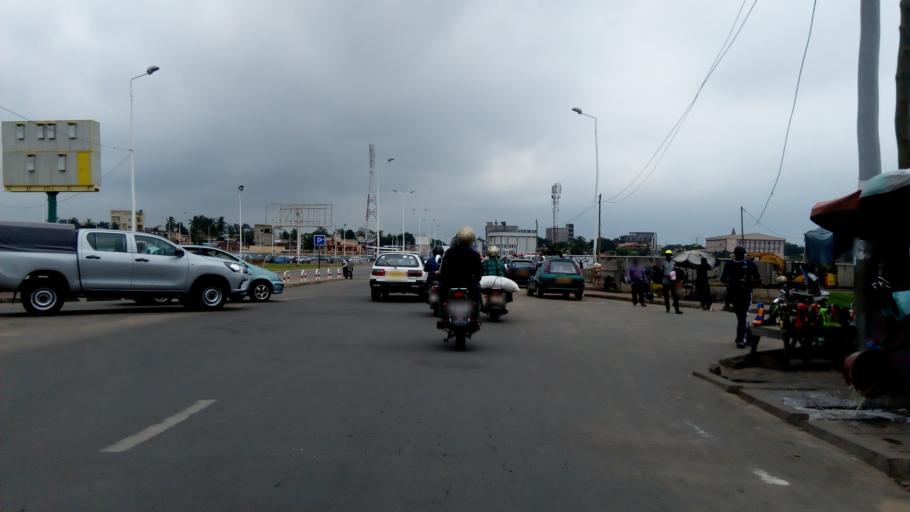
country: TG
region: Maritime
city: Lome
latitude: 6.1440
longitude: 1.2299
